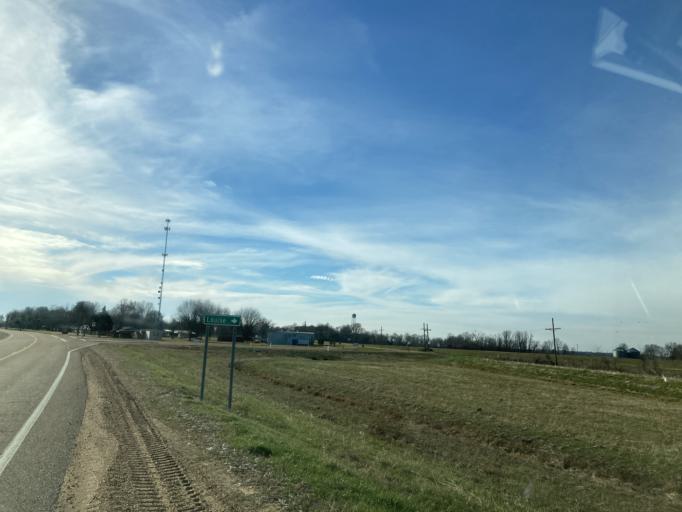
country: US
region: Mississippi
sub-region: Humphreys County
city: Belzoni
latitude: 32.9911
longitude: -90.5889
